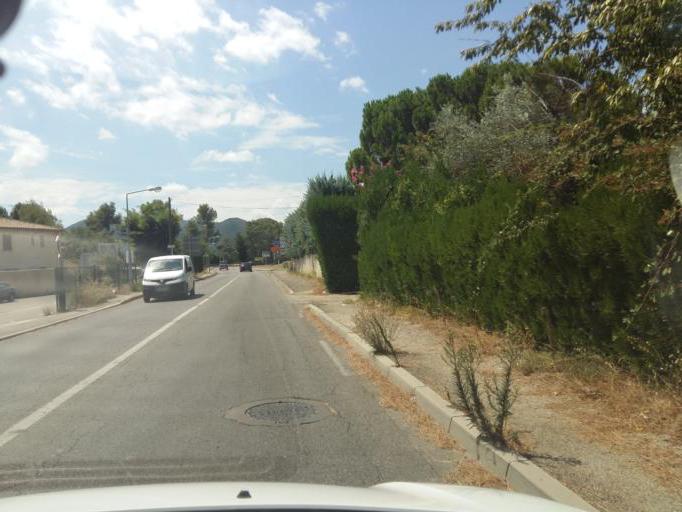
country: FR
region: Provence-Alpes-Cote d'Azur
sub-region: Departement du Vaucluse
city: Vaison-la-Romaine
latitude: 44.2468
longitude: 5.0921
